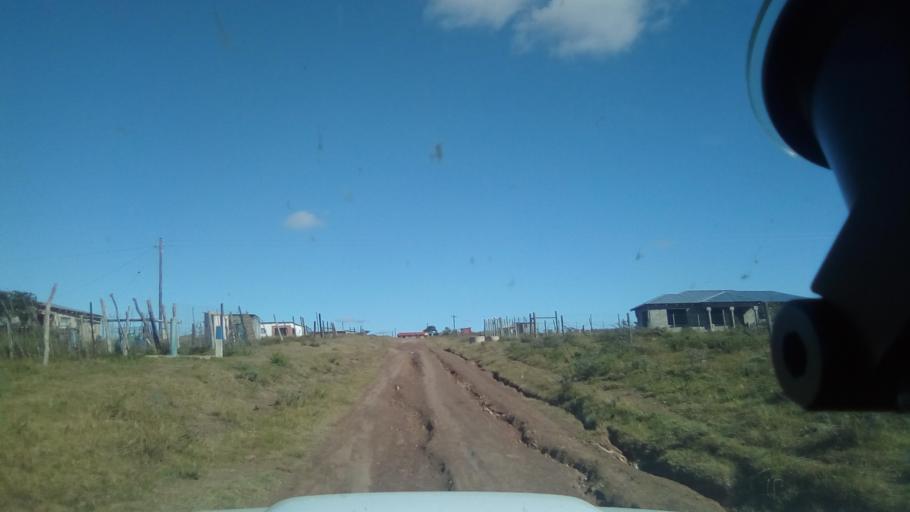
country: ZA
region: Eastern Cape
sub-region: Buffalo City Metropolitan Municipality
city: Bhisho
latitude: -32.7799
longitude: 27.3381
